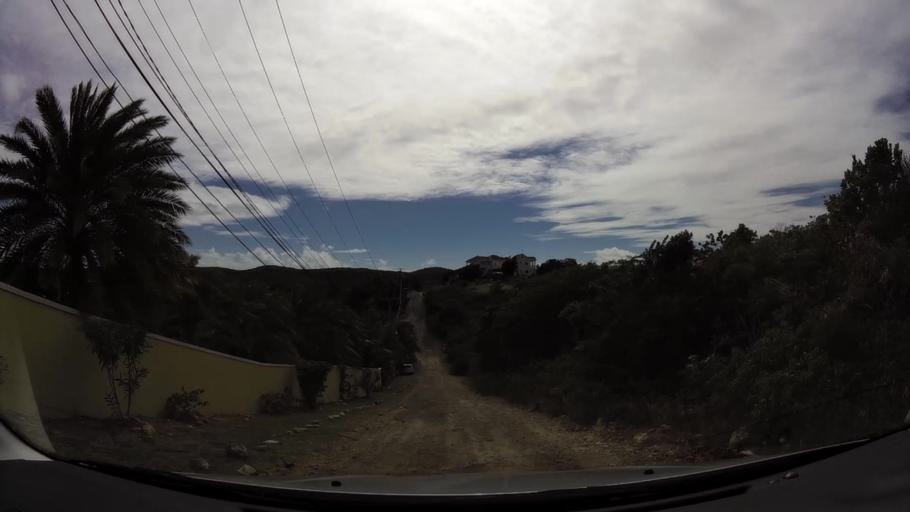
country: AG
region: Saint Peter
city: Parham
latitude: 17.0679
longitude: -61.6984
